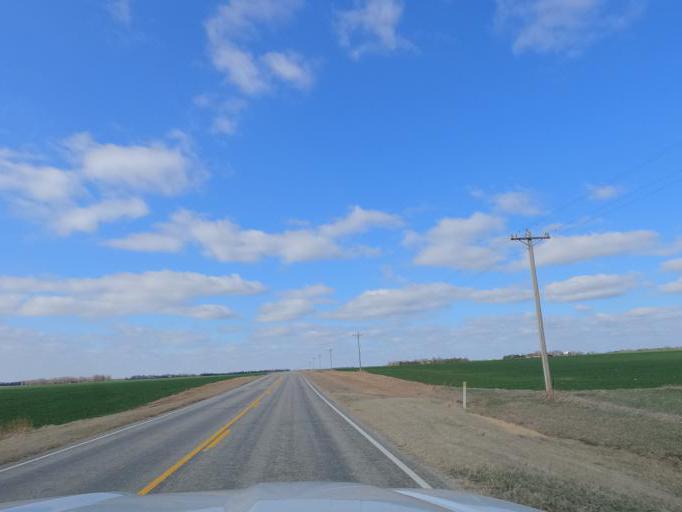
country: US
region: Kansas
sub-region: McPherson County
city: Inman
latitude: 38.2229
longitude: -97.8485
